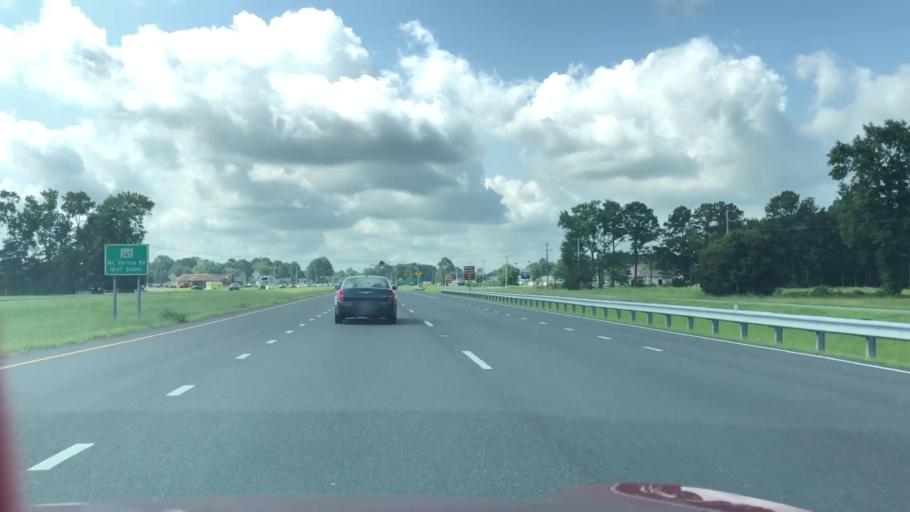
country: US
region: Maryland
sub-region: Somerset County
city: Princess Anne
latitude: 38.2185
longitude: -75.6989
